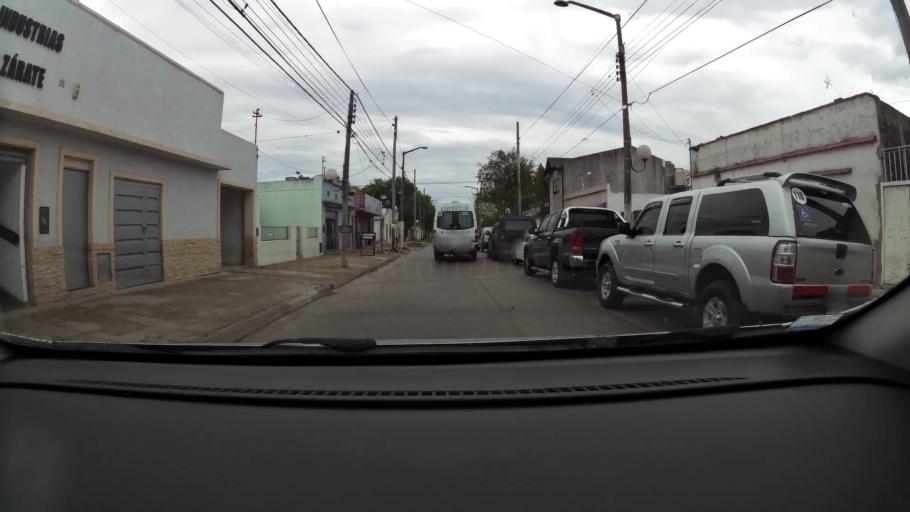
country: AR
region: Buenos Aires
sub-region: Partido de Zarate
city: Zarate
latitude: -34.0821
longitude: -59.0361
